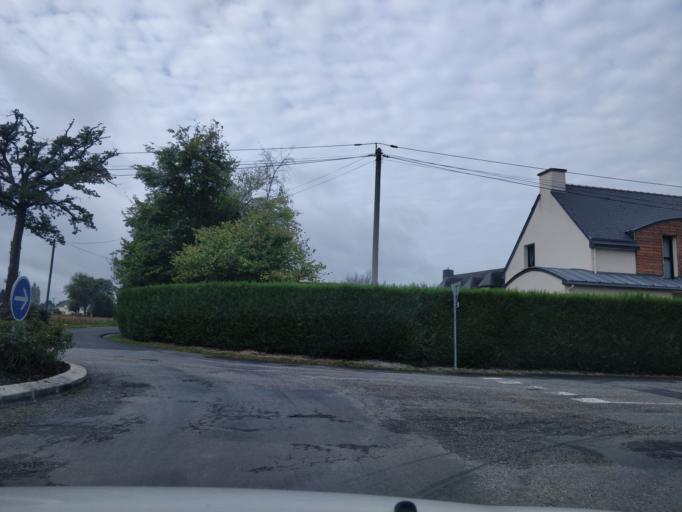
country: FR
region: Brittany
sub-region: Departement d'Ille-et-Vilaine
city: La Bouexiere
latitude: 48.1789
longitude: -1.4330
